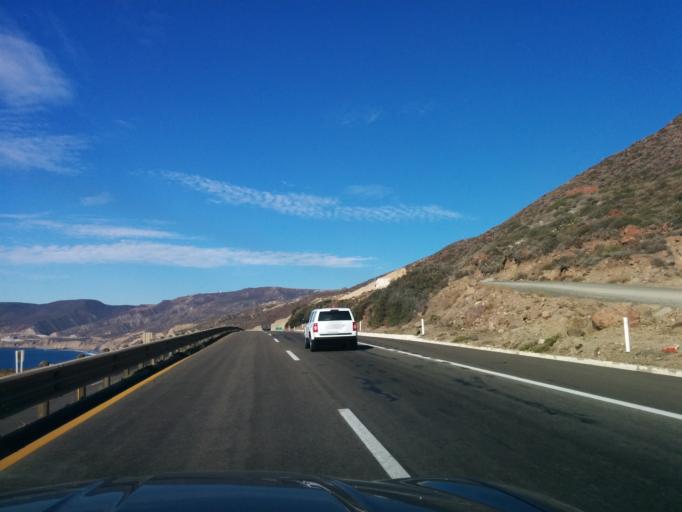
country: MX
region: Baja California
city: El Sauzal
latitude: 31.9358
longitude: -116.7536
